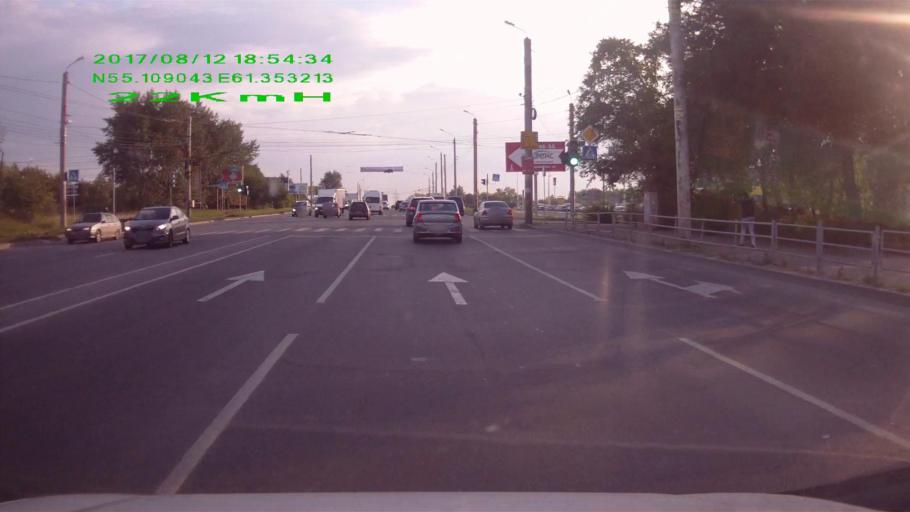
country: RU
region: Chelyabinsk
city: Novosineglazovskiy
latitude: 55.1047
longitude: 61.3465
